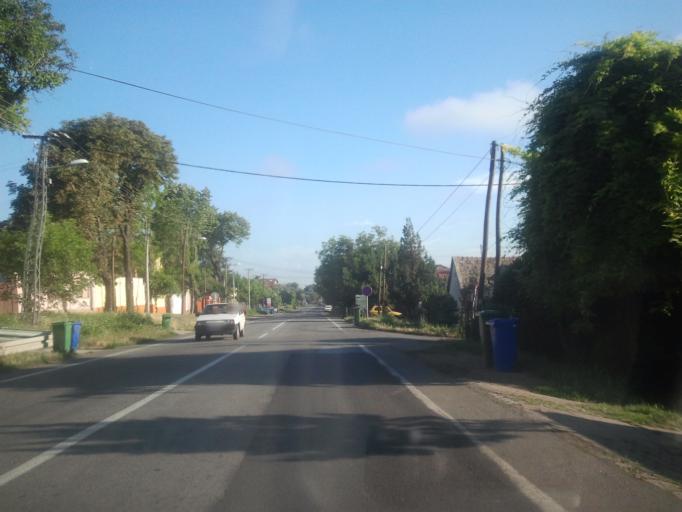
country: RS
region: Autonomna Pokrajina Vojvodina
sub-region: Juznobacki Okrug
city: Petrovaradin
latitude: 45.2371
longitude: 19.8846
